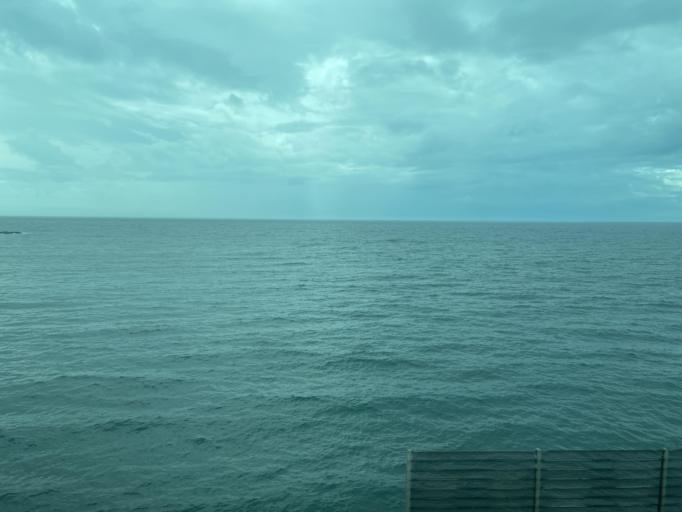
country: JP
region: Niigata
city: Kashiwazaki
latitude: 37.3536
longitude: 138.5069
